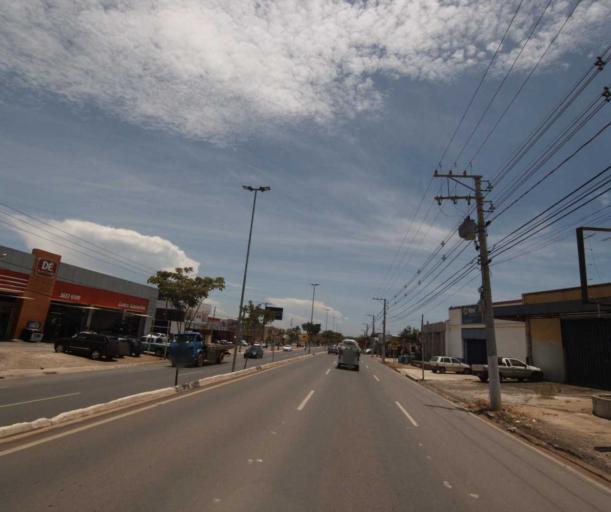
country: BR
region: Mato Grosso
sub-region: Varzea Grande
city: Varzea Grande
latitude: -15.6146
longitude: -56.1255
